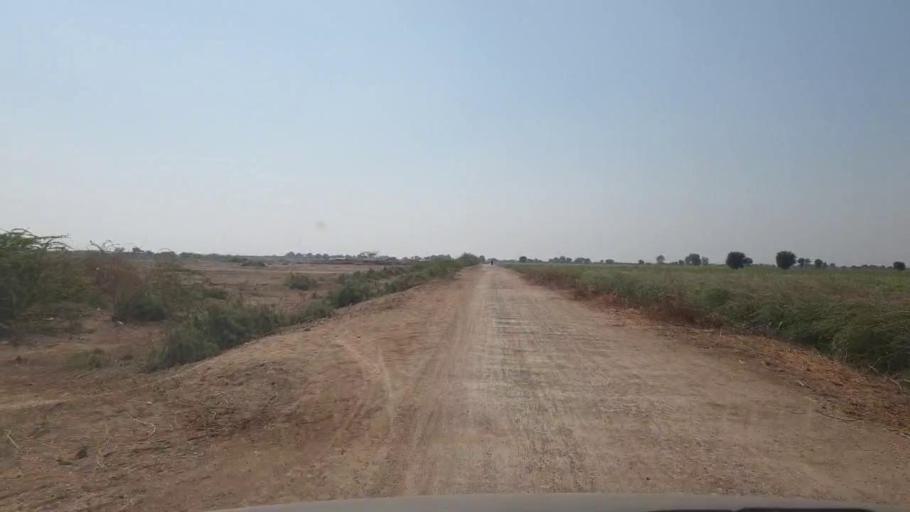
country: PK
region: Sindh
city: Digri
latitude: 25.2327
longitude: 69.2222
